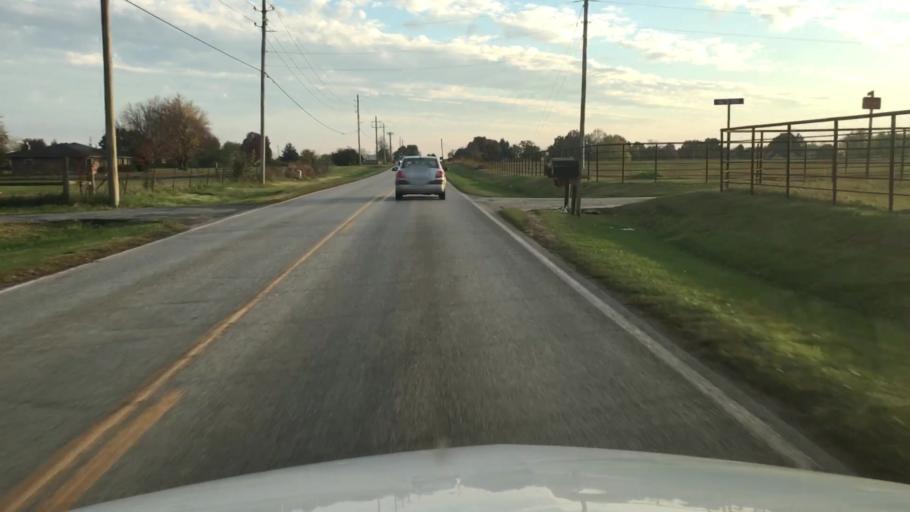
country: US
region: Arkansas
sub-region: Washington County
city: Elm Springs
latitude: 36.2232
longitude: -94.2304
